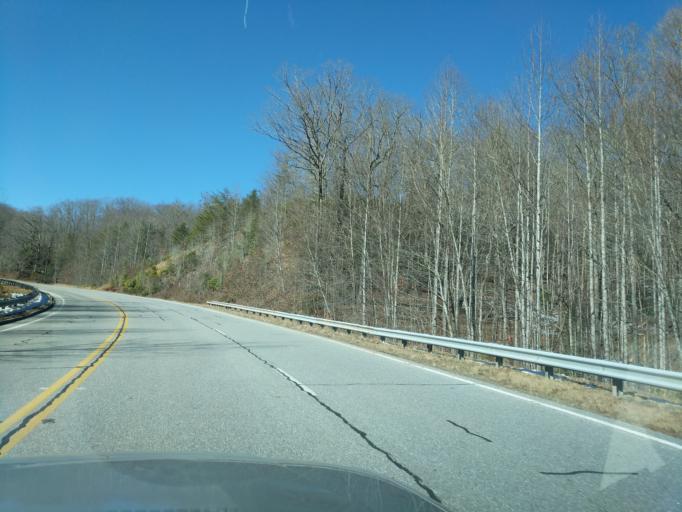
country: US
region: Georgia
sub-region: Towns County
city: Hiawassee
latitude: 34.9073
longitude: -83.6120
